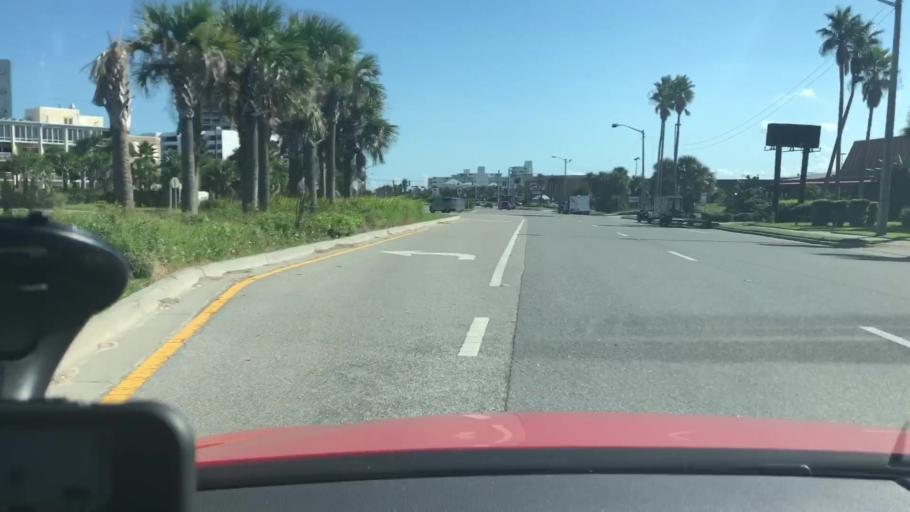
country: US
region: Florida
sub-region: Volusia County
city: Holly Hill
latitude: 29.2711
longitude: -81.0298
